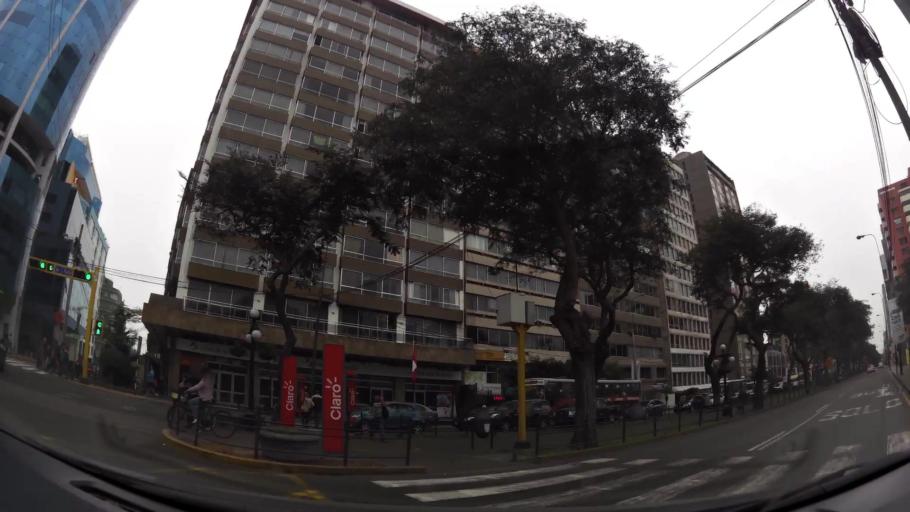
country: PE
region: Lima
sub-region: Lima
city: San Isidro
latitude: -12.1190
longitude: -77.0304
